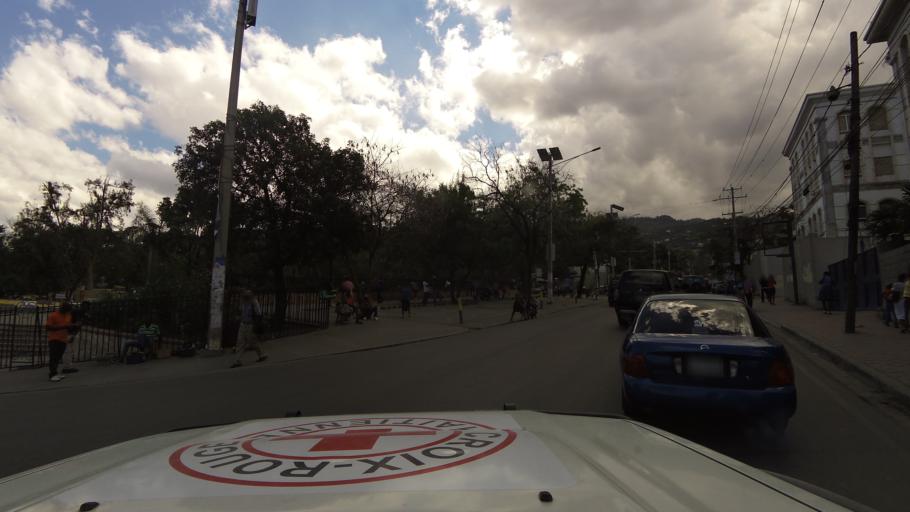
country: HT
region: Ouest
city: Petionville
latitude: 18.5132
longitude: -72.2830
